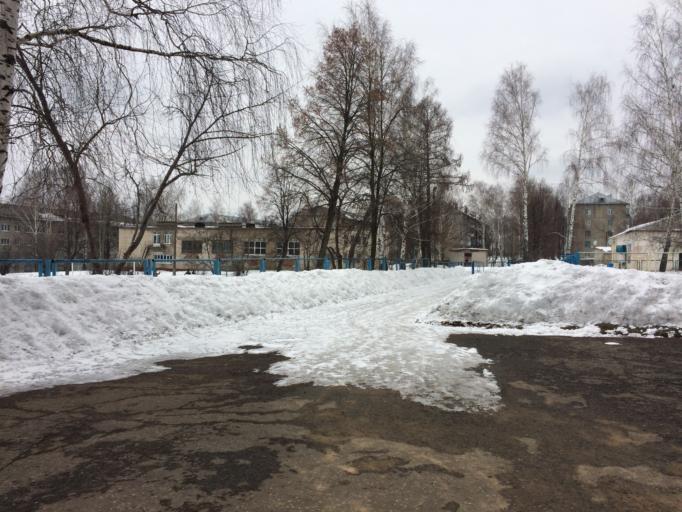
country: RU
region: Mariy-El
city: Mochalishche
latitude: 56.5426
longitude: 48.4054
